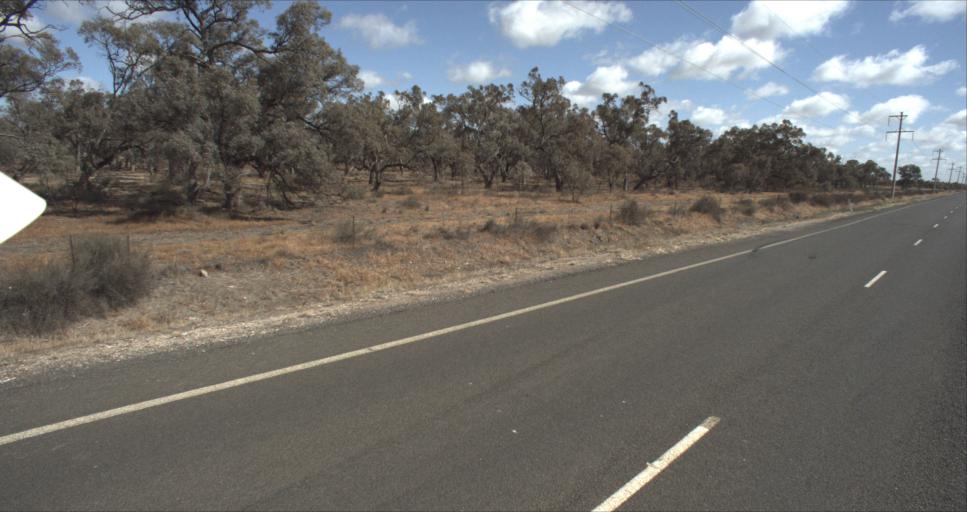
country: AU
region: New South Wales
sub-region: Murrumbidgee Shire
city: Darlington Point
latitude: -34.5244
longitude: 146.1751
